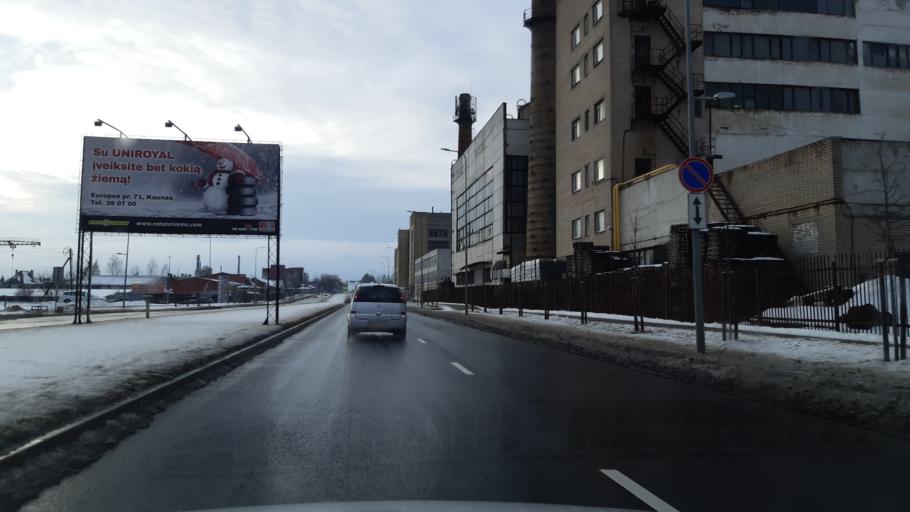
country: LT
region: Kauno apskritis
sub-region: Kaunas
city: Aleksotas
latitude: 54.8754
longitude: 23.8992
